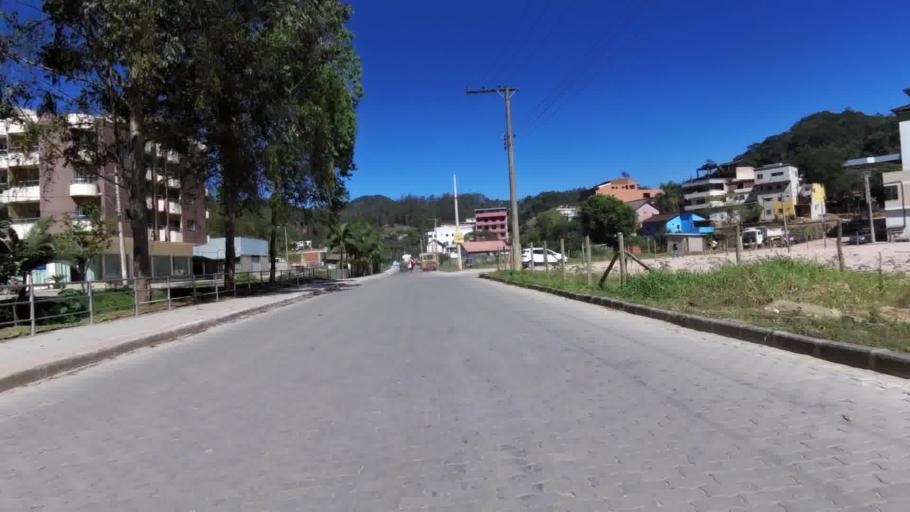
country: BR
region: Espirito Santo
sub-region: Vargem Alta
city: Vargem Alta
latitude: -20.6728
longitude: -41.0082
